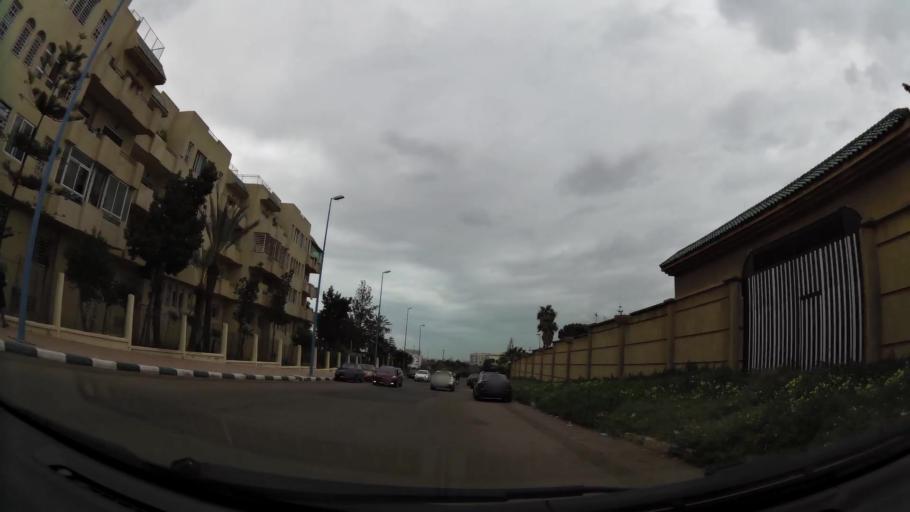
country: MA
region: Grand Casablanca
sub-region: Casablanca
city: Casablanca
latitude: 33.5468
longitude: -7.6367
